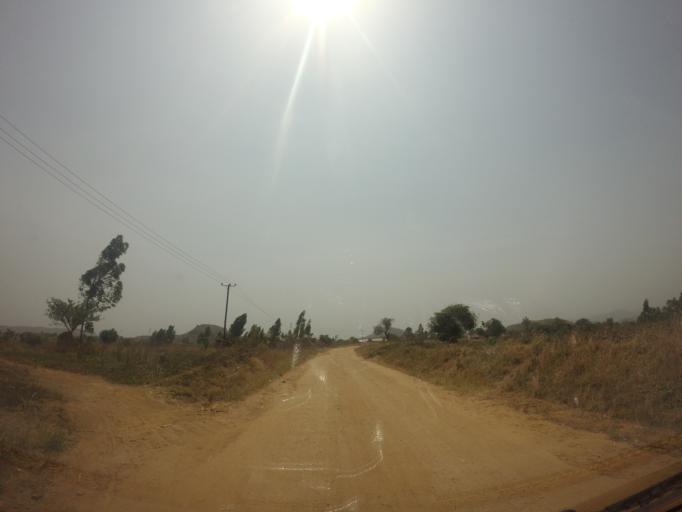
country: UG
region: Northern Region
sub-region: Arua District
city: Arua
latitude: 2.9410
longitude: 30.9804
